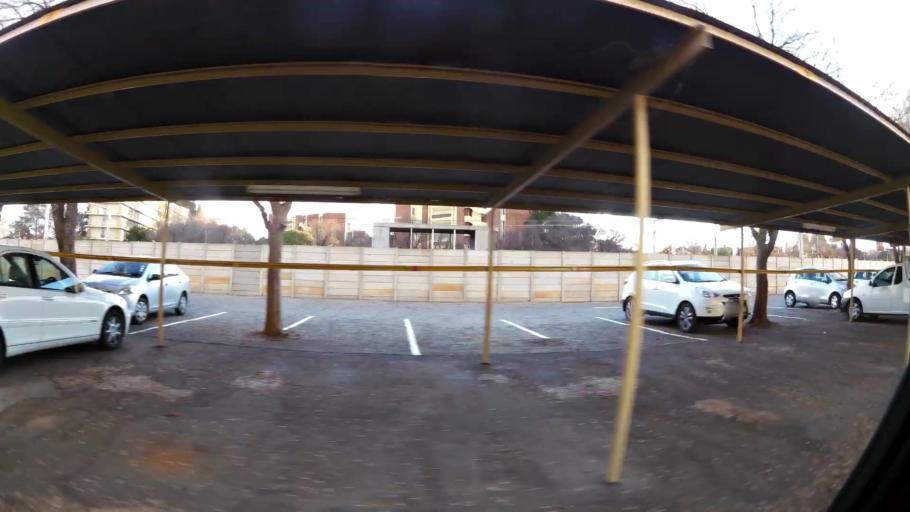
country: ZA
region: North-West
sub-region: Dr Kenneth Kaunda District Municipality
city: Potchefstroom
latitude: -26.6886
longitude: 27.0906
